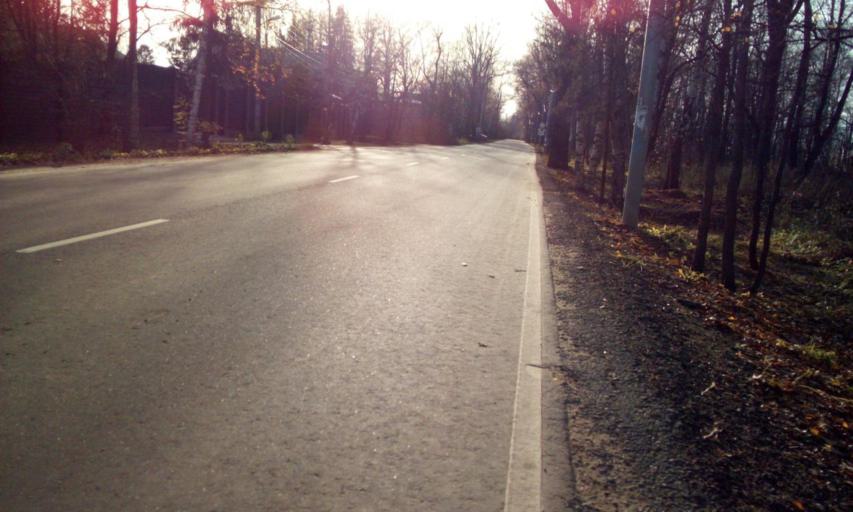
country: RU
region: Moskovskaya
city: Aprelevka
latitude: 55.5811
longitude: 37.1202
